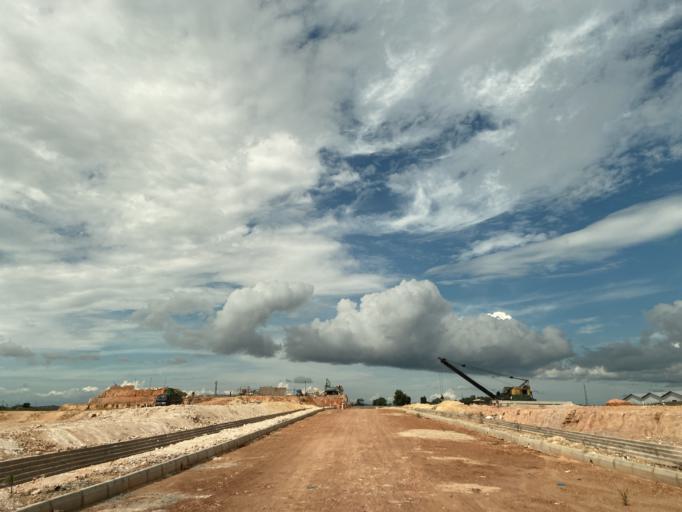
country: SG
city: Singapore
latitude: 1.0214
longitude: 103.9520
